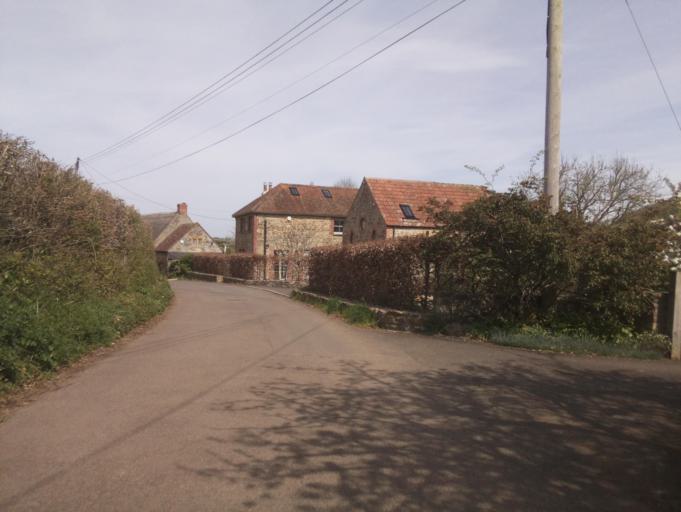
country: GB
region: England
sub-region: Dorset
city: Sherborne
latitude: 50.9805
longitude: -2.5322
